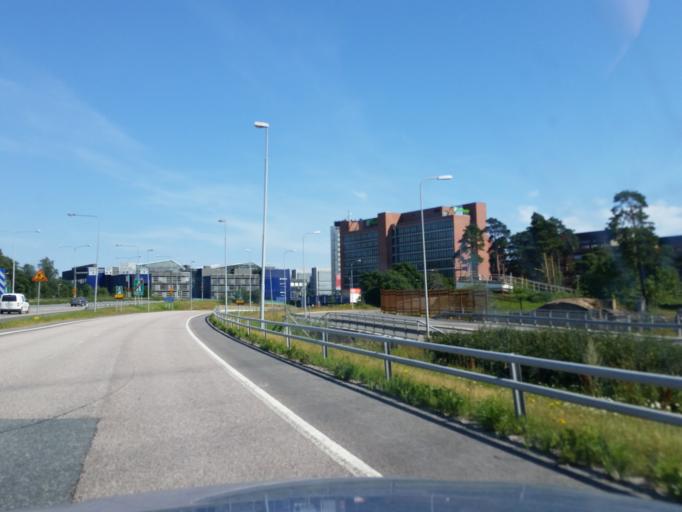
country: FI
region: Uusimaa
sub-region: Helsinki
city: Helsinki
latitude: 60.1667
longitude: 24.9061
